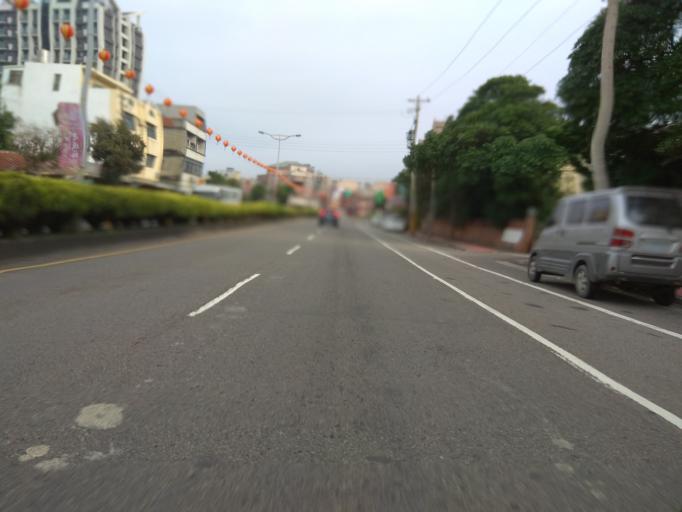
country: TW
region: Taiwan
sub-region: Hsinchu
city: Hsinchu
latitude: 24.8369
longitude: 120.9299
